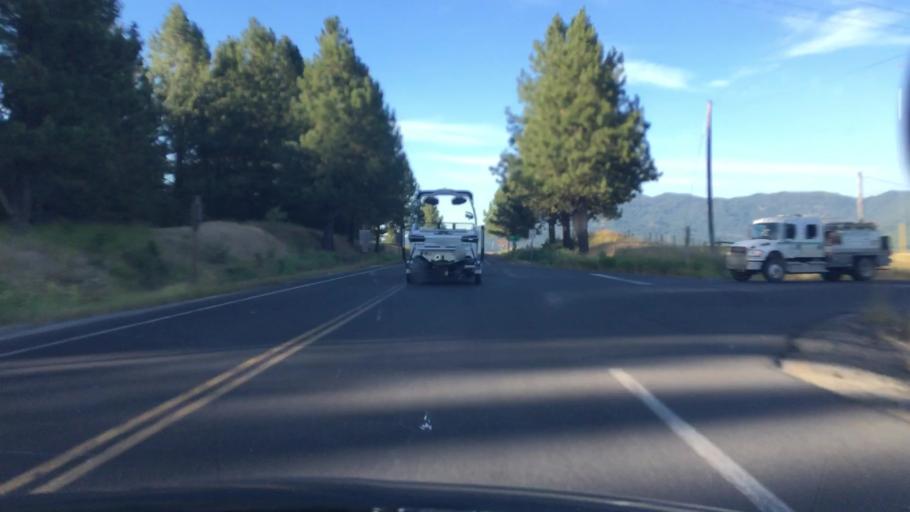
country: US
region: Idaho
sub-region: Valley County
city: Cascade
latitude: 44.5277
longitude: -116.0414
